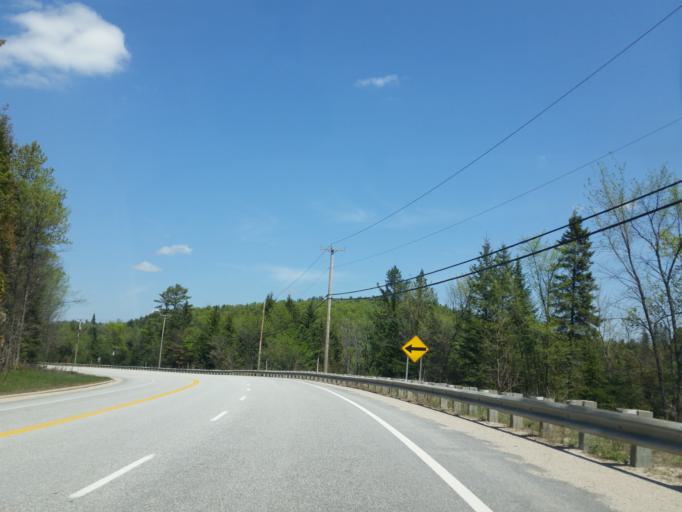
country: CA
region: Quebec
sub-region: Outaouais
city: Wakefield
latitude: 45.6608
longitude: -75.9262
